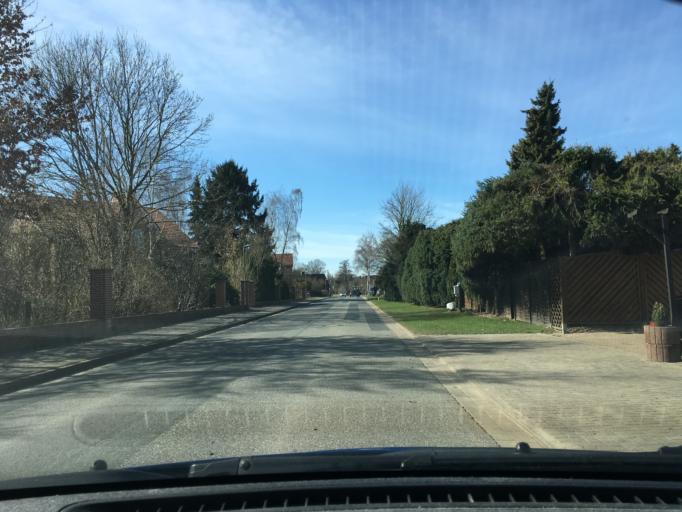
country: DE
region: Lower Saxony
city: Winsen
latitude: 53.3876
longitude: 10.2332
